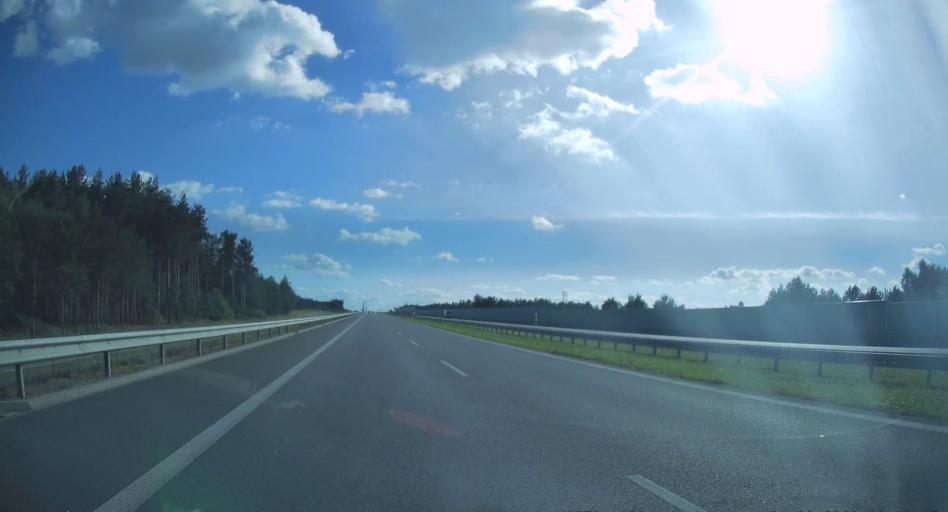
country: PL
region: Masovian Voivodeship
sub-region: Powiat szydlowiecki
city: Oronsko
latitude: 51.3073
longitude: 21.0052
